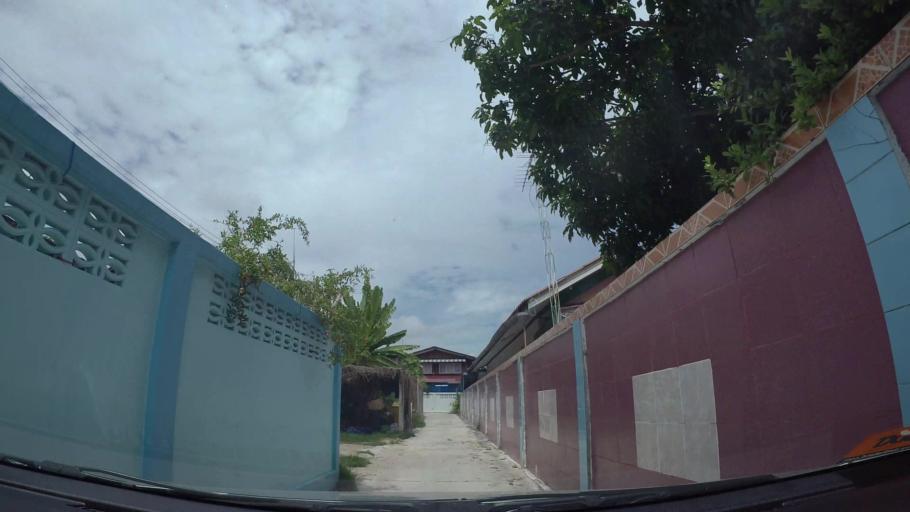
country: TH
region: Chon Buri
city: Sattahip
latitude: 12.6788
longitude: 100.8965
